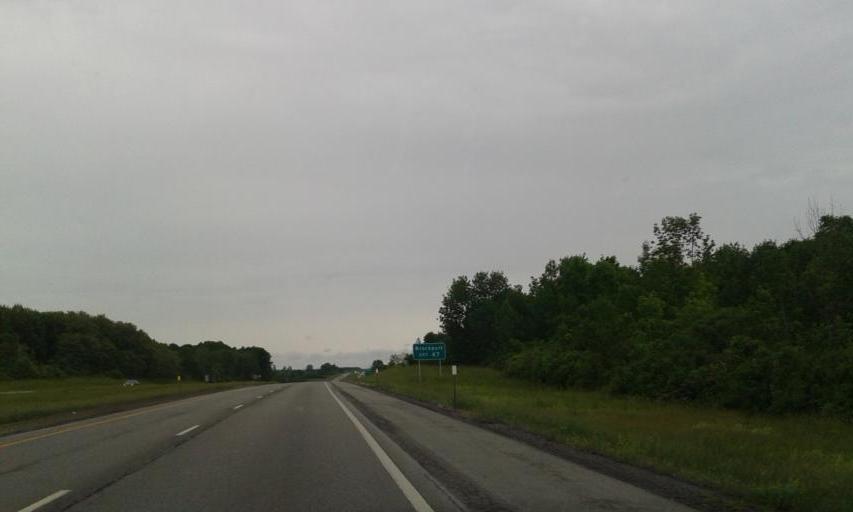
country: US
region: New York
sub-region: Genesee County
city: Bergen
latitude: 43.0287
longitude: -77.9373
